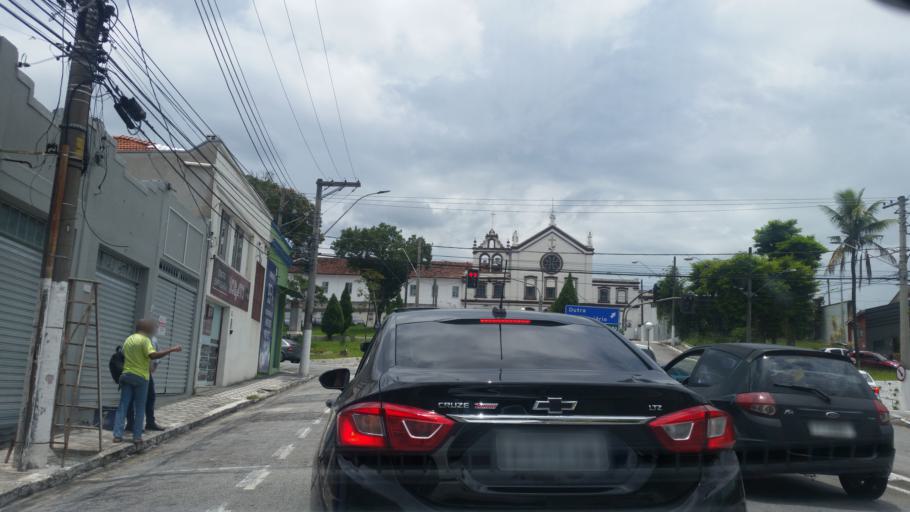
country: BR
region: Sao Paulo
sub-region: Taubate
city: Taubate
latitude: -23.0217
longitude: -45.5520
